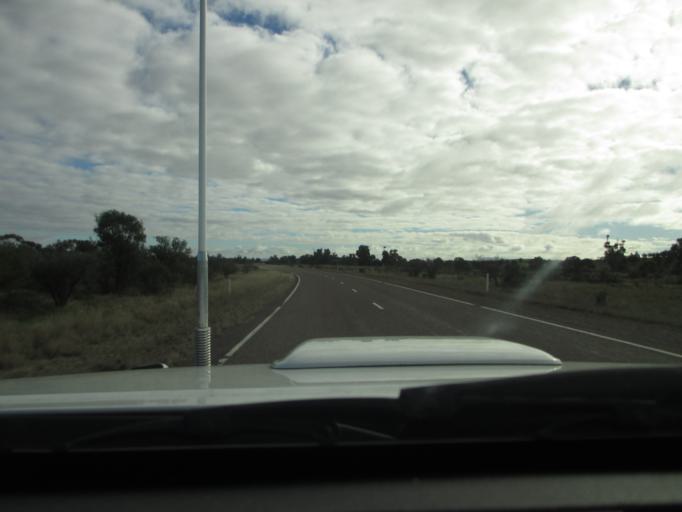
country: AU
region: South Australia
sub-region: Flinders Ranges
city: Quorn
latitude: -32.4885
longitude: 138.5459
